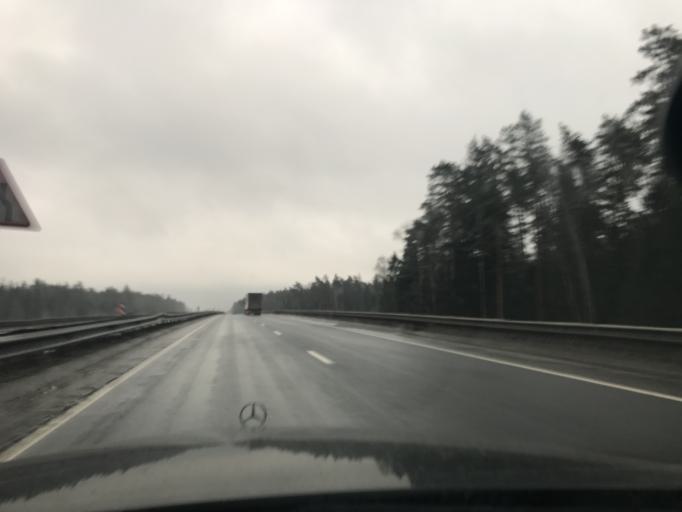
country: RU
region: Vladimir
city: Krasnyy Oktyabr'
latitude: 56.2175
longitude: 41.4438
